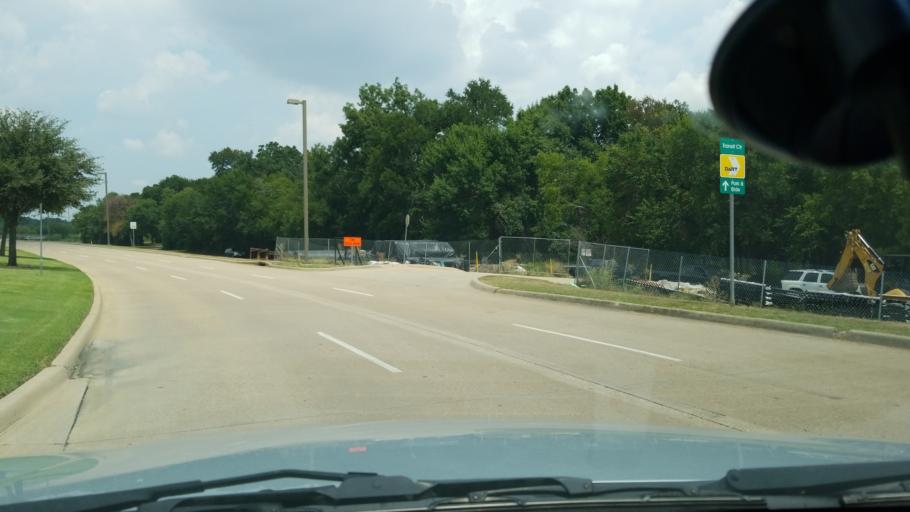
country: US
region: Texas
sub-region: Dallas County
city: Irving
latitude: 32.8623
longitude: -96.9259
